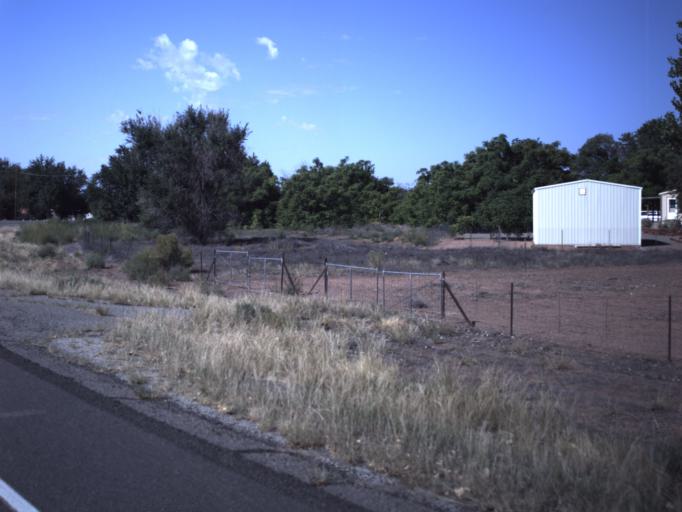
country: US
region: Utah
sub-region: San Juan County
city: Blanding
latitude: 37.2838
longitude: -109.5488
